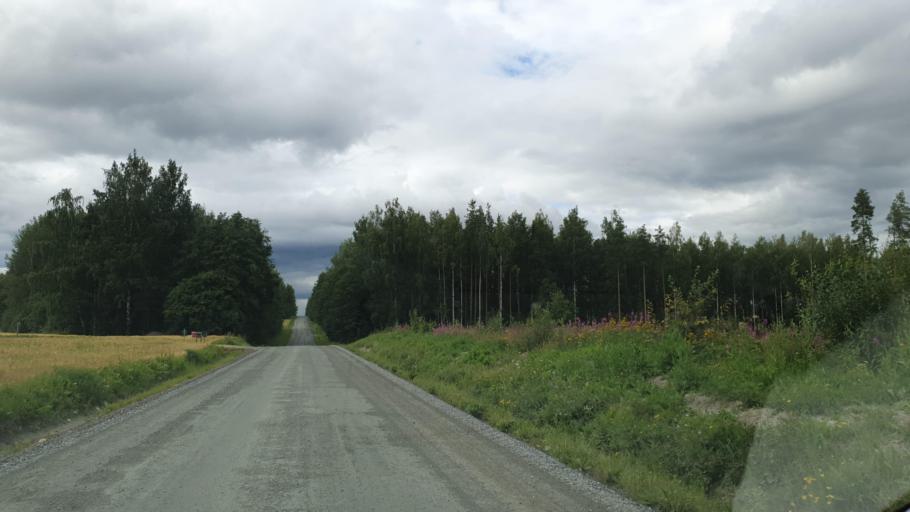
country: FI
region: Northern Savo
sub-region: Ylae-Savo
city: Iisalmi
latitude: 63.5195
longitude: 27.0997
